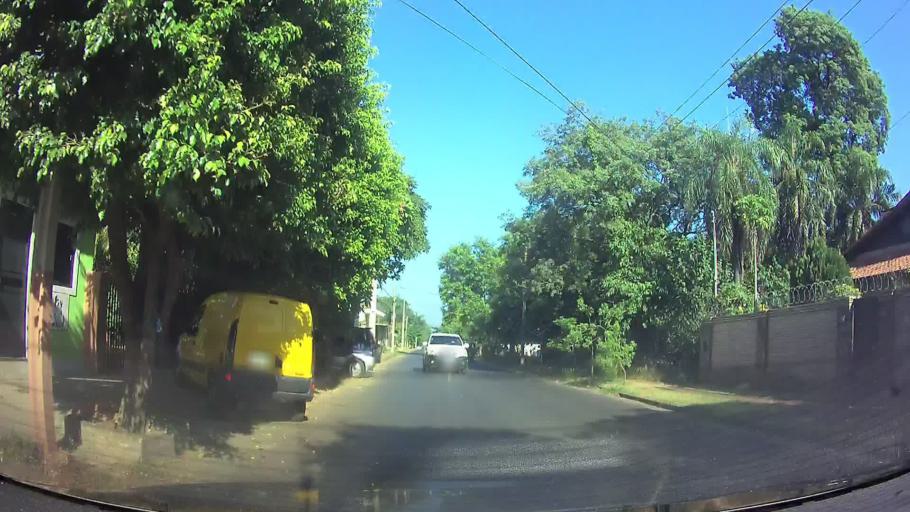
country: PY
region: Central
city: San Lorenzo
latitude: -25.2749
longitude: -57.5055
